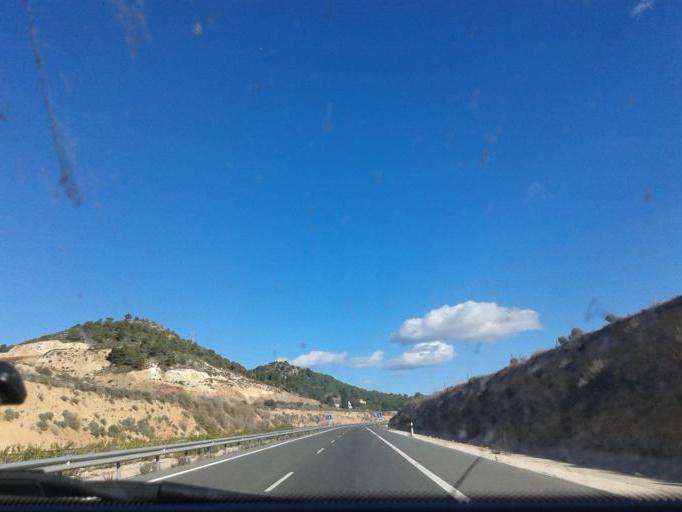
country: ES
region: Valencia
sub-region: Provincia de Alicante
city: Biar
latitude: 38.5917
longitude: -0.7471
